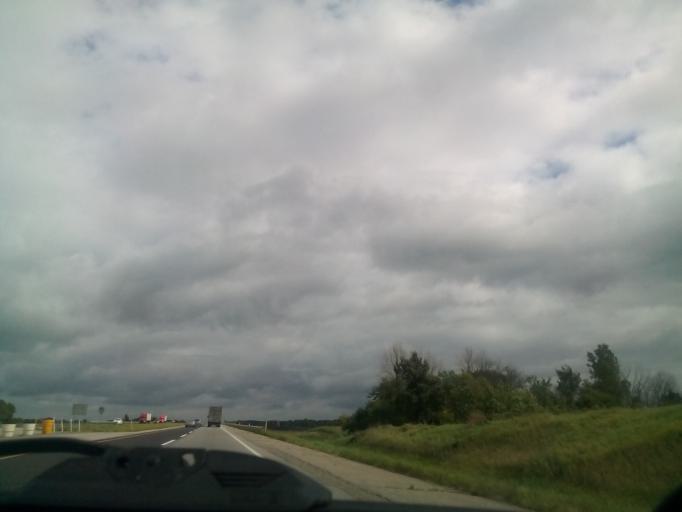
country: US
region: Indiana
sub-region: Steuben County
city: Fremont
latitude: 41.7155
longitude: -84.9523
